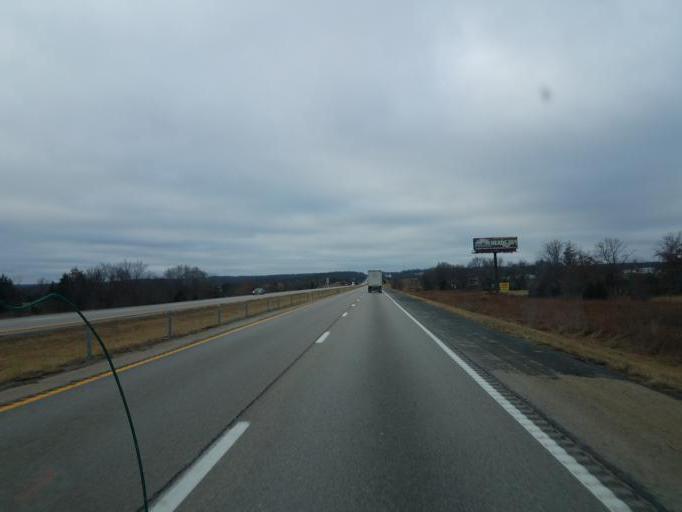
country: US
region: Missouri
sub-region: Laclede County
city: Lebanon
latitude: 37.5786
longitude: -92.7532
